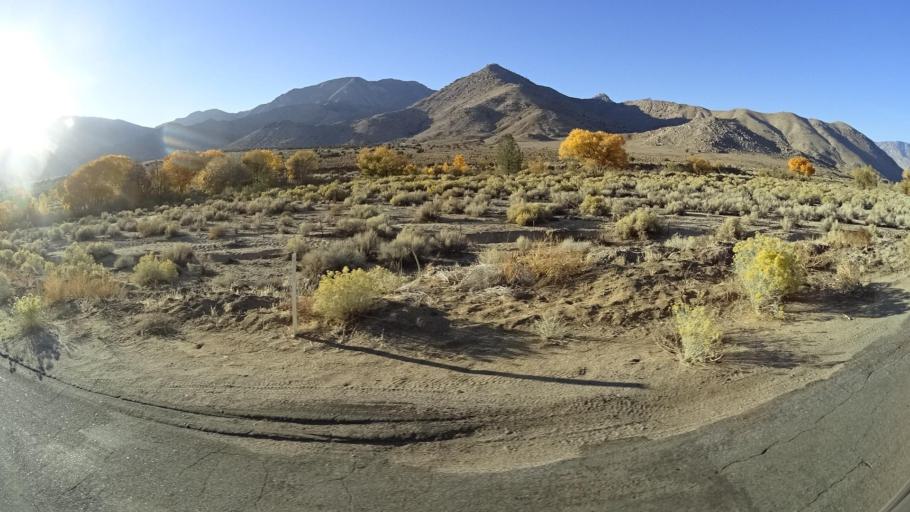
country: US
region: California
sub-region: Kern County
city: Weldon
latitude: 35.5795
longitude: -118.2488
